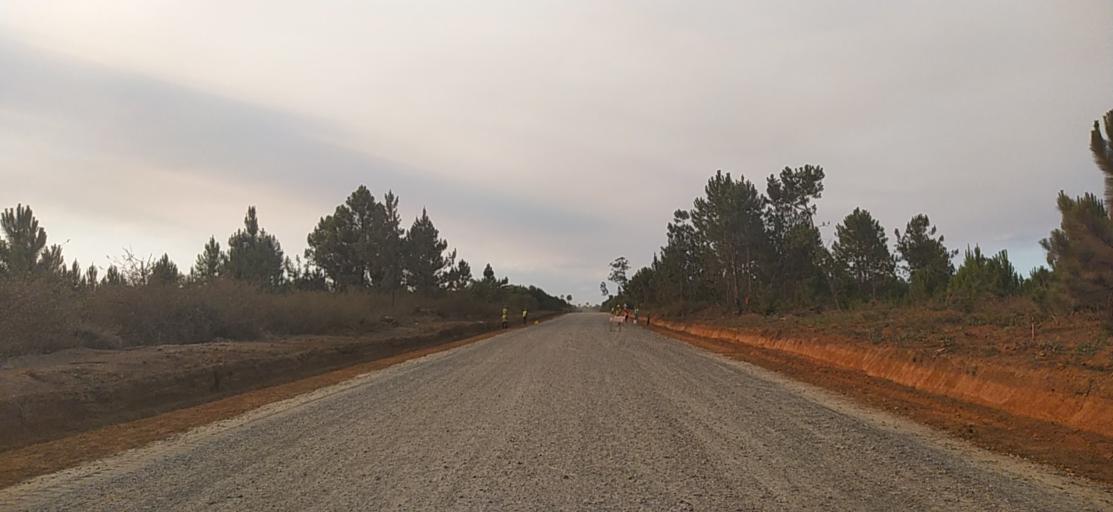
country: MG
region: Alaotra Mangoro
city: Moramanga
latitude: -18.5406
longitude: 48.2592
